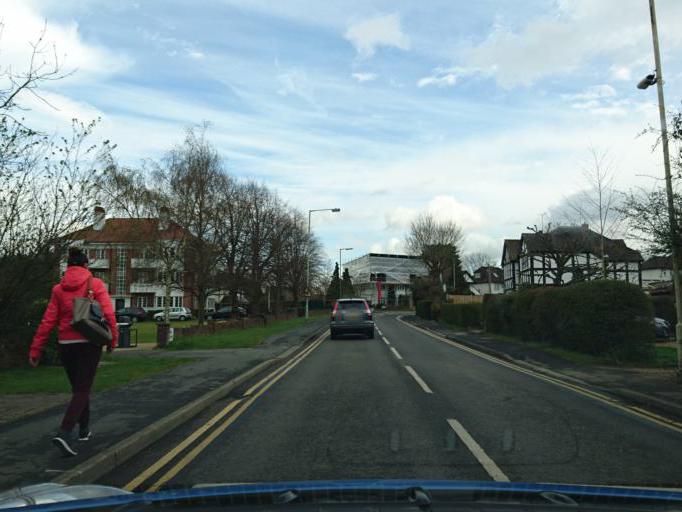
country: GB
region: England
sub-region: Hertfordshire
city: Borehamwood
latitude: 51.6525
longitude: -0.2817
